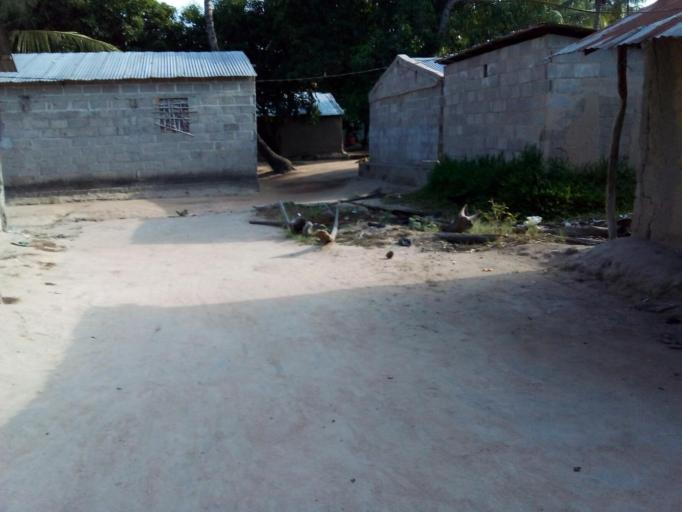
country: MZ
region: Zambezia
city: Quelimane
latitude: -17.6052
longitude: 36.8243
